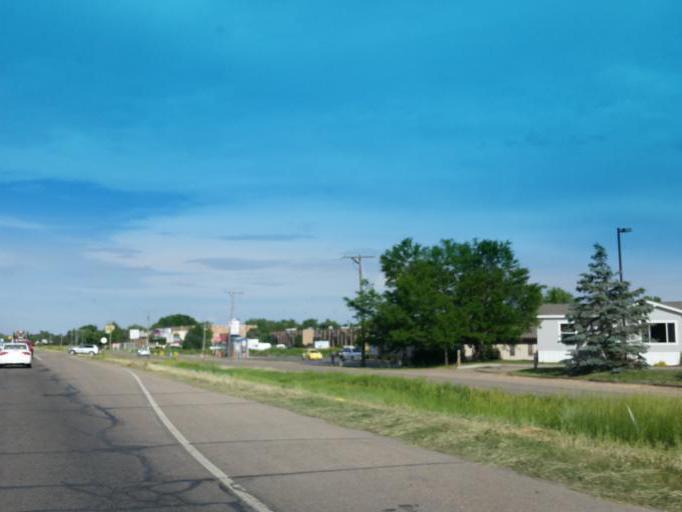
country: US
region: Colorado
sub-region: Larimer County
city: Fort Collins
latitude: 40.5809
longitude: -105.0464
